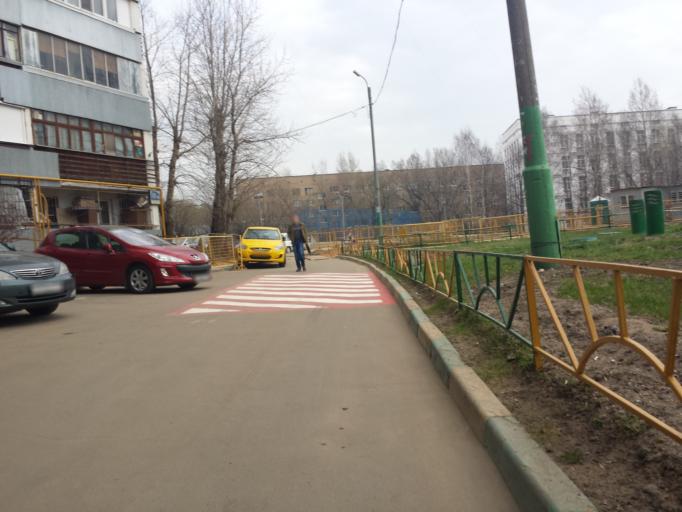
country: RU
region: Moskovskaya
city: Novogireyevo
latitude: 55.7481
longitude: 37.8279
